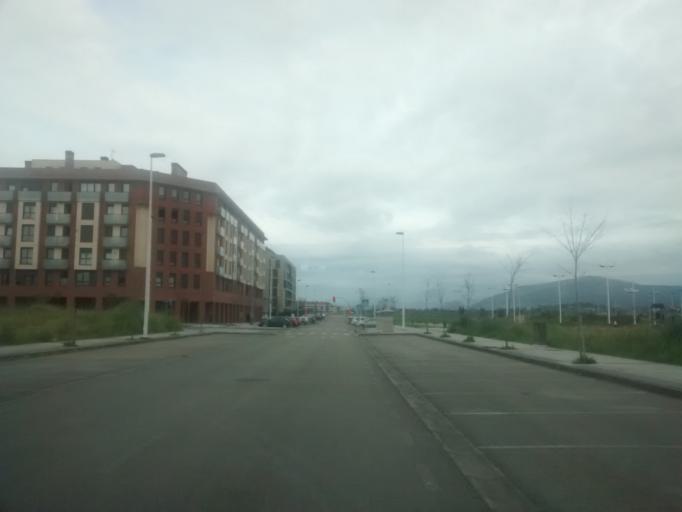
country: ES
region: Cantabria
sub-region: Provincia de Cantabria
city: Camargo
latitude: 43.4410
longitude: -3.8540
